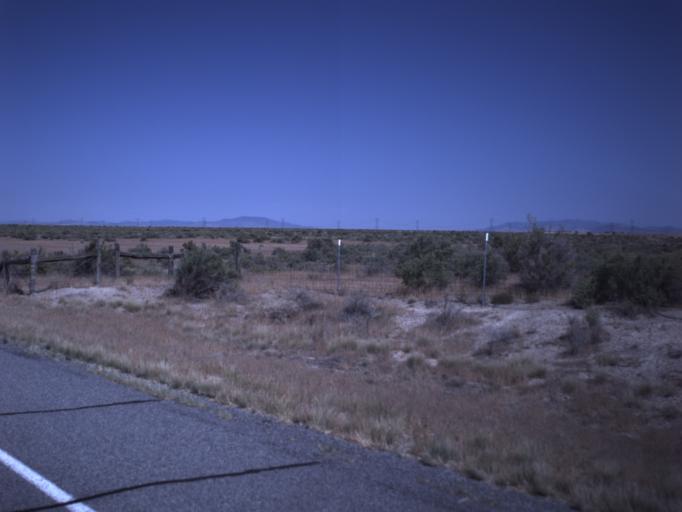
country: US
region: Utah
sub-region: Millard County
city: Delta
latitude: 39.4666
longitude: -112.4429
